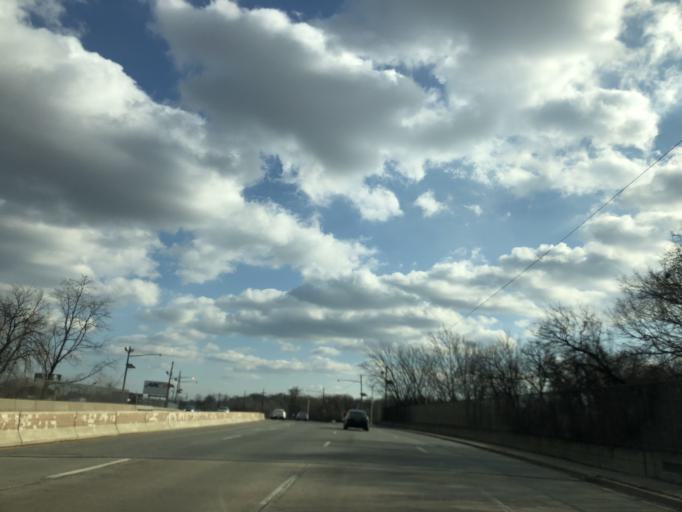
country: US
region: New Jersey
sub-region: Camden County
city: Camden
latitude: 39.9422
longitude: -75.1057
